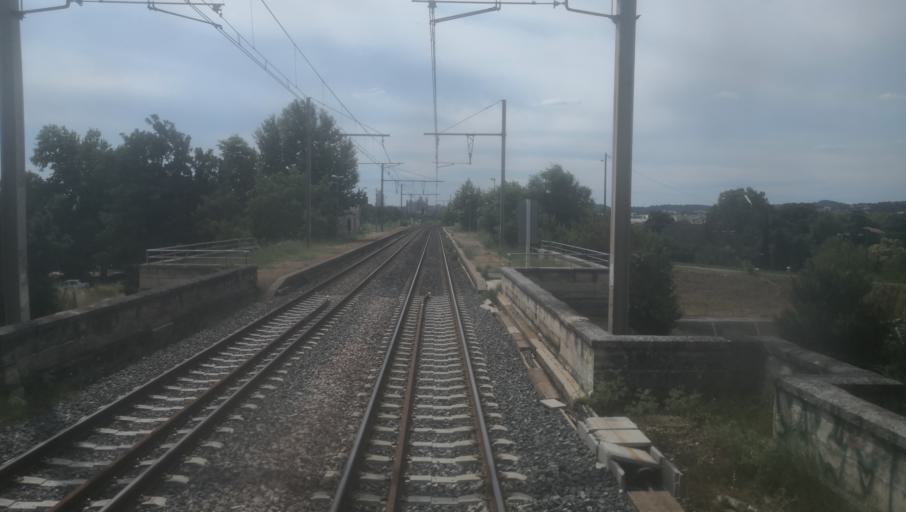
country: FR
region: Languedoc-Roussillon
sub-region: Departement du Gard
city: Beaucaire
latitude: 43.8021
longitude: 4.6479
